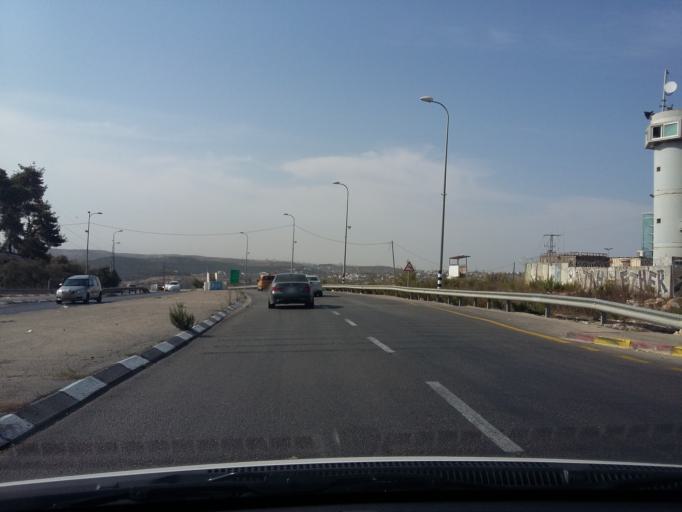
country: PS
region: West Bank
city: Shuyukh al `Arrub
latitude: 31.6454
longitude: 35.1317
